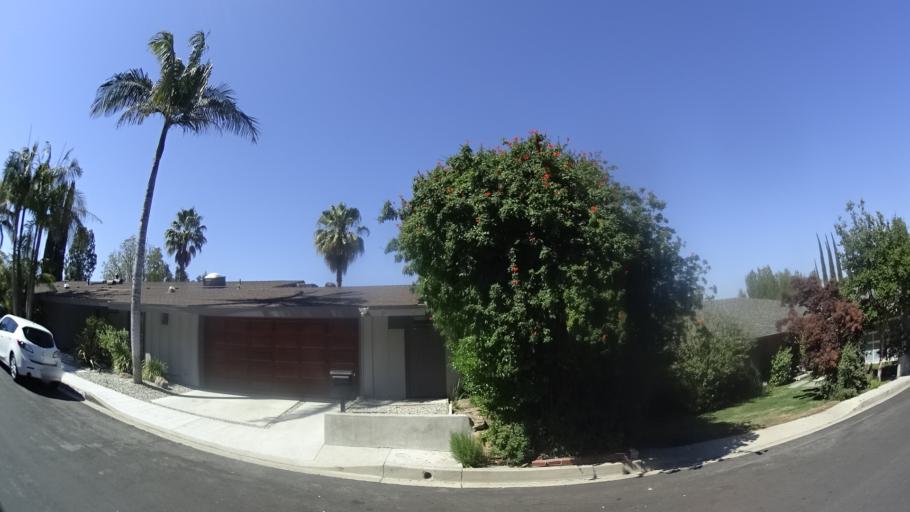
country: US
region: California
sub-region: Los Angeles County
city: Sherman Oaks
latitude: 34.1352
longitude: -118.4837
